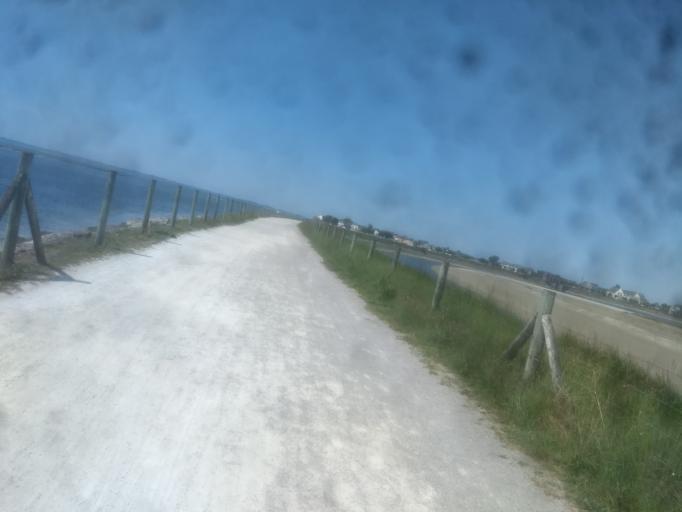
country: FR
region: Picardie
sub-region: Departement de la Somme
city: Le Crotoy
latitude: 50.2130
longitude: 1.6398
